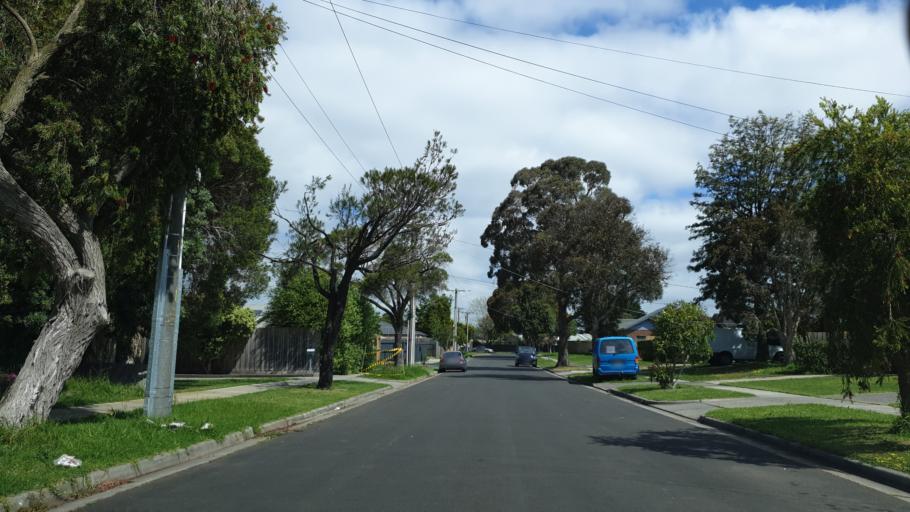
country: AU
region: Victoria
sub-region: Casey
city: Cranbourne
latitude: -38.1029
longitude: 145.2896
